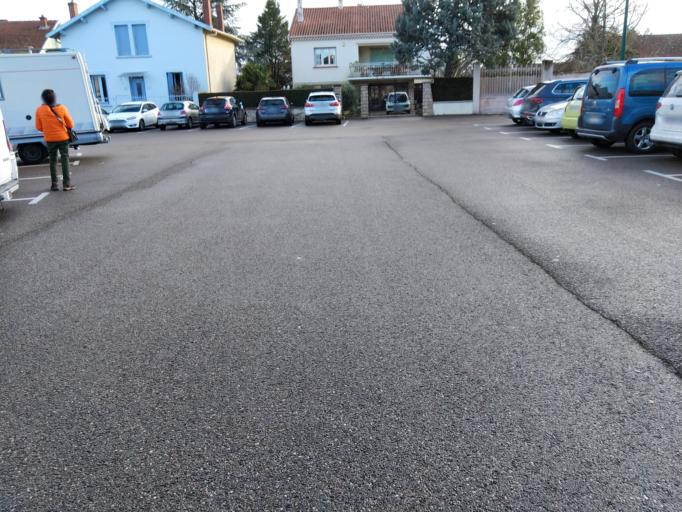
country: FR
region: Rhone-Alpes
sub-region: Departement de l'Isere
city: Chanas
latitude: 45.2925
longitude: 4.8156
